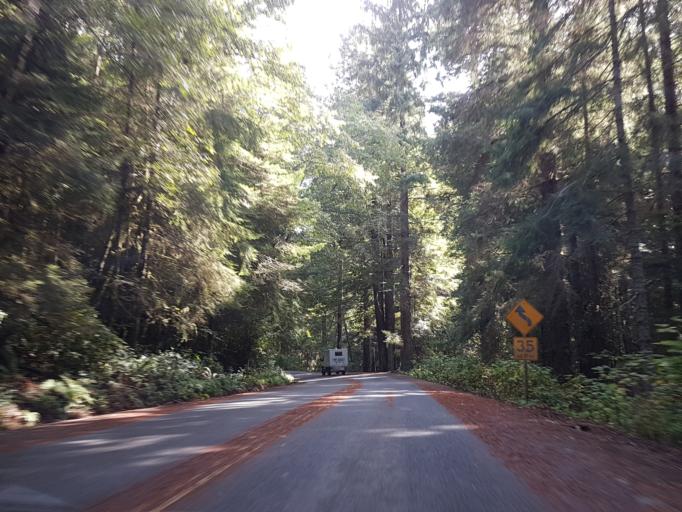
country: US
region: California
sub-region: Del Norte County
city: Bertsch-Oceanview
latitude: 41.4537
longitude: -124.0429
